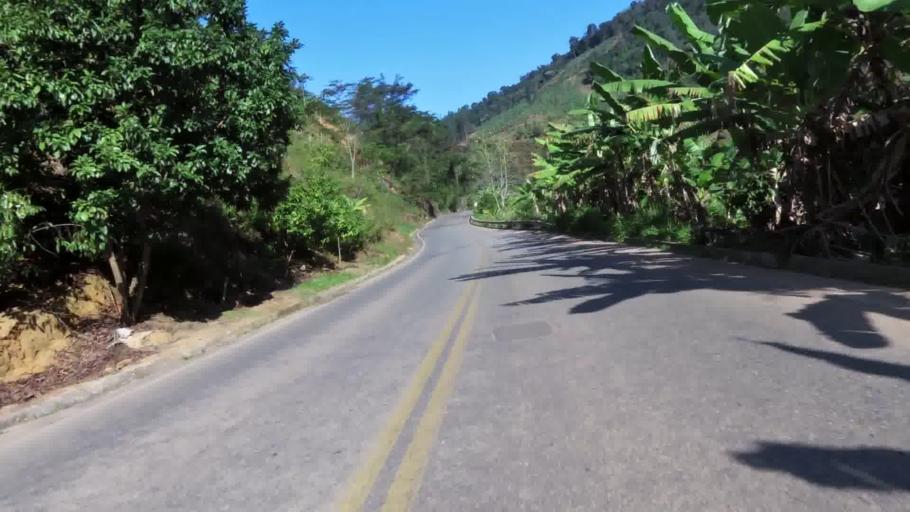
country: BR
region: Espirito Santo
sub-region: Alfredo Chaves
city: Alfredo Chaves
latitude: -20.6227
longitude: -40.7775
